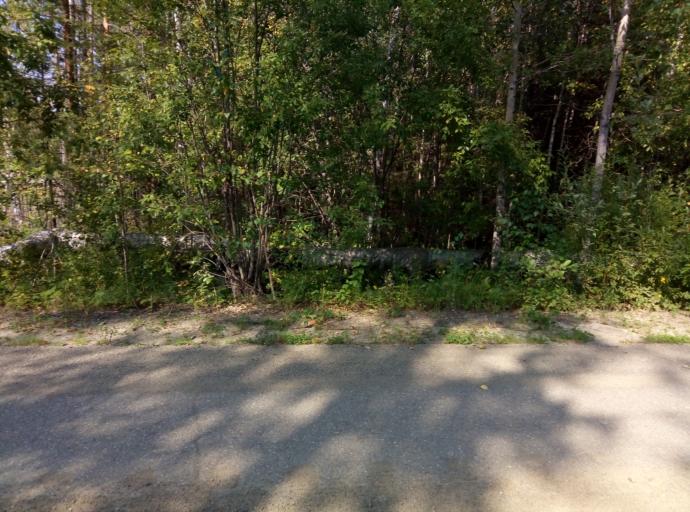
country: RU
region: Sverdlovsk
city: Krasnotur'insk
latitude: 59.6881
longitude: 60.1932
